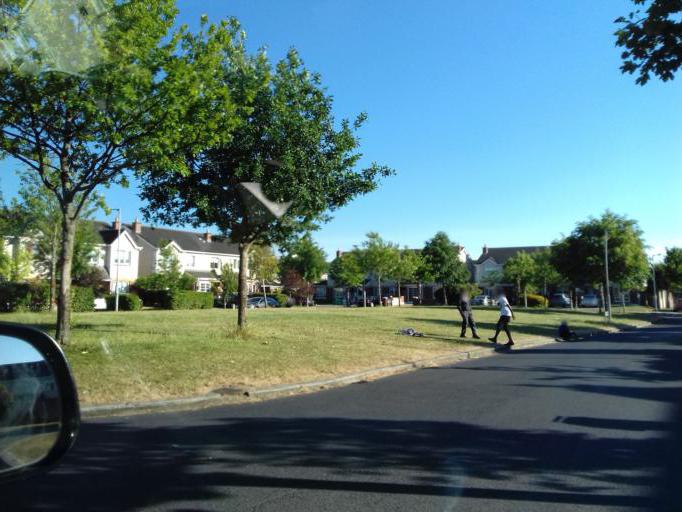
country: IE
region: Leinster
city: Hartstown
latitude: 53.3955
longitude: -6.4260
